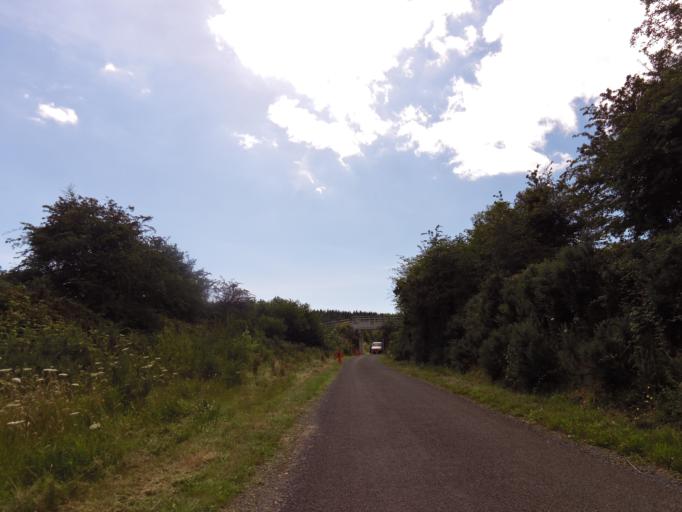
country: IE
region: Leinster
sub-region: Kilkenny
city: Mooncoin
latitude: 52.2406
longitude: -7.2655
